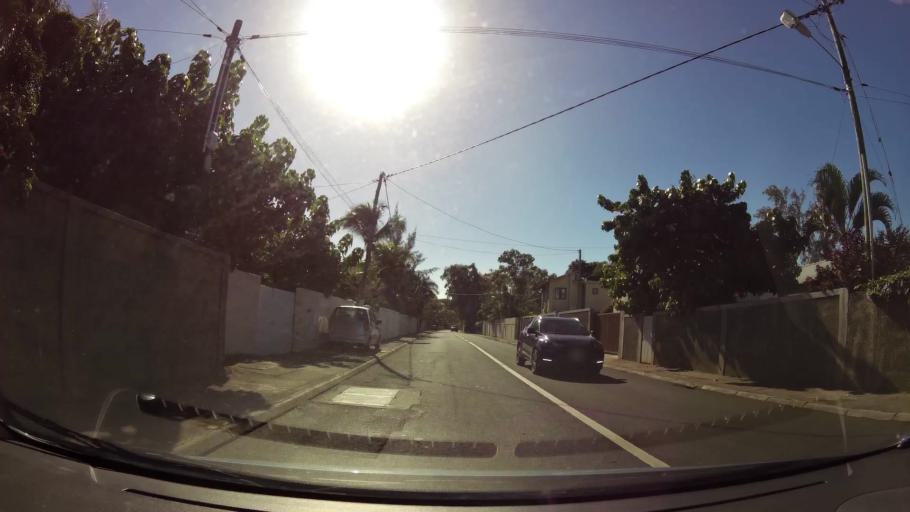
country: MU
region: Black River
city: Tamarin
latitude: -20.3322
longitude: 57.3692
